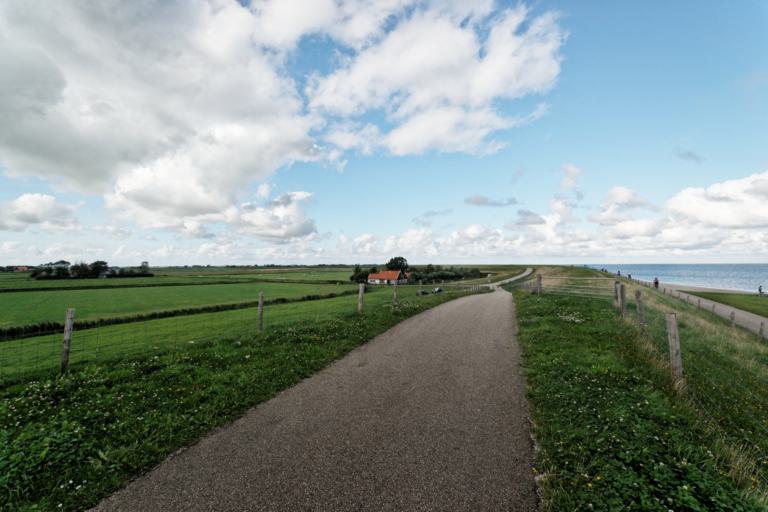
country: NL
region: North Holland
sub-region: Gemeente Texel
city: Den Burg
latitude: 53.0789
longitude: 4.8961
